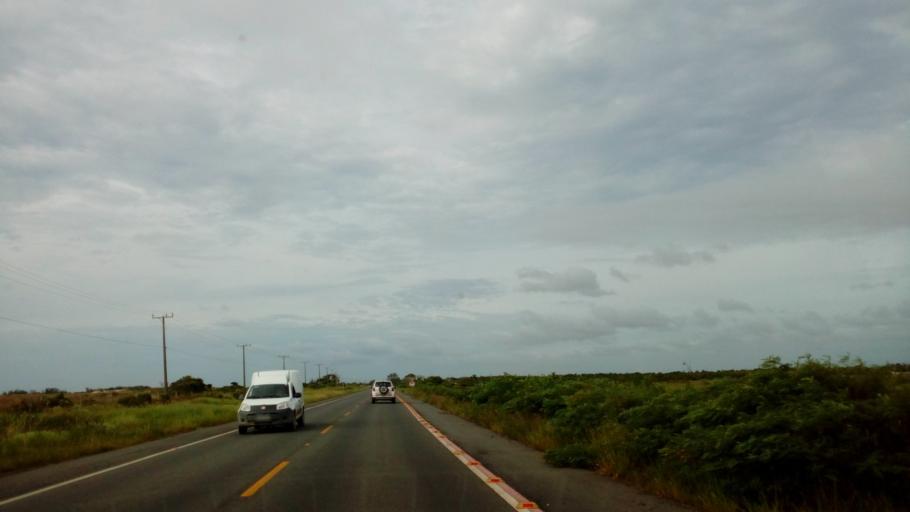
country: BR
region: Santa Catarina
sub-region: Laguna
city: Laguna
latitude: -28.5828
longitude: -48.8288
